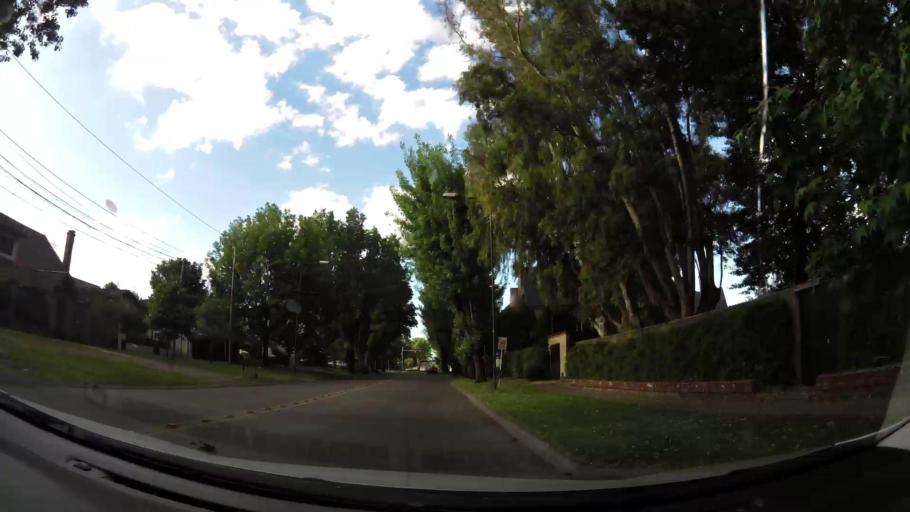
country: AR
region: Buenos Aires
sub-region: Partido de San Isidro
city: San Isidro
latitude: -34.4865
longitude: -58.5565
